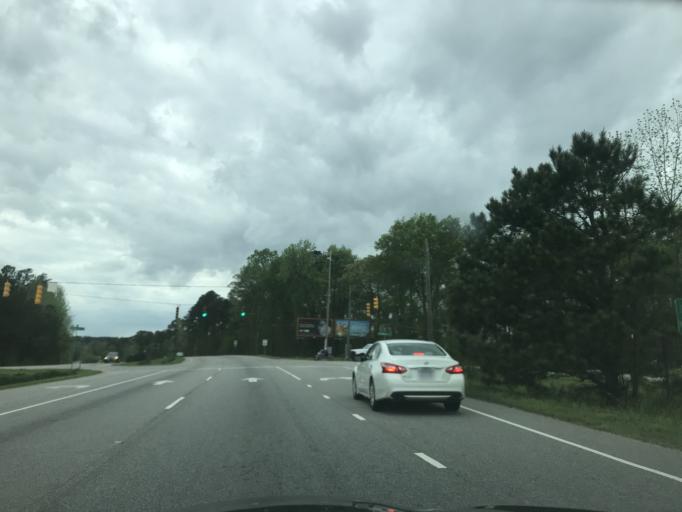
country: US
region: North Carolina
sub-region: Wake County
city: Knightdale
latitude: 35.7961
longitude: -78.5337
